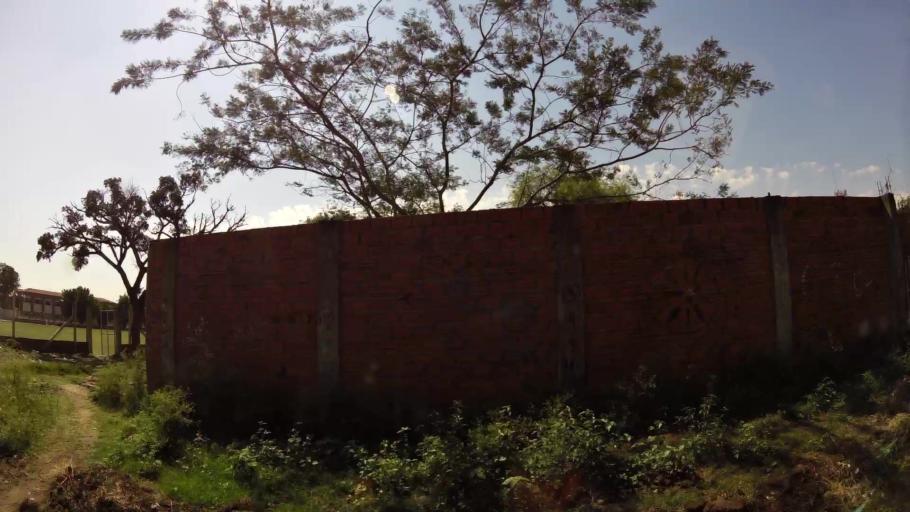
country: BO
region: Santa Cruz
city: Santa Cruz de la Sierra
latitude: -17.7296
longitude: -63.1606
